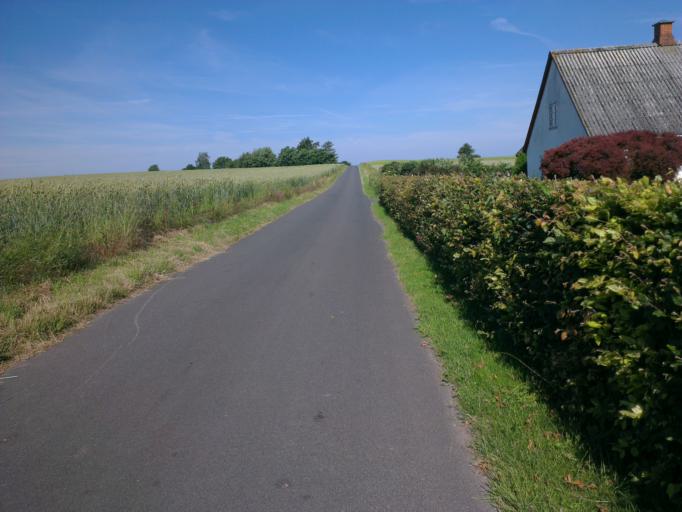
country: DK
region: Capital Region
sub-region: Frederikssund Kommune
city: Skibby
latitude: 55.7862
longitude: 11.8743
